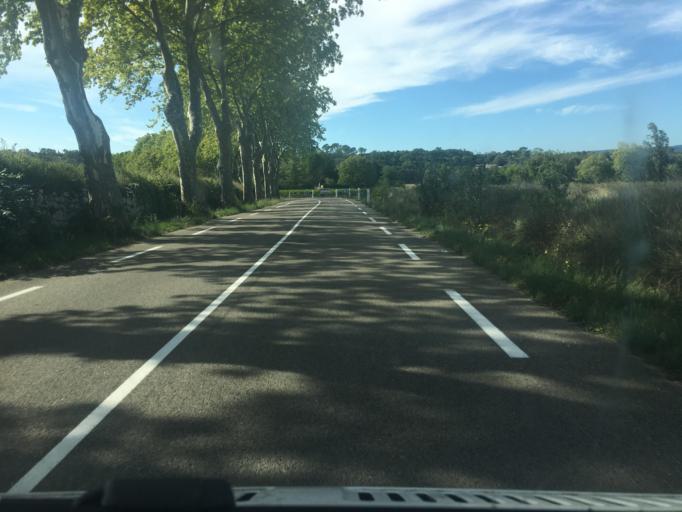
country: FR
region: Languedoc-Roussillon
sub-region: Departement du Gard
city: Saint-Quentin-la-Poterie
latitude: 44.0211
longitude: 4.4398
